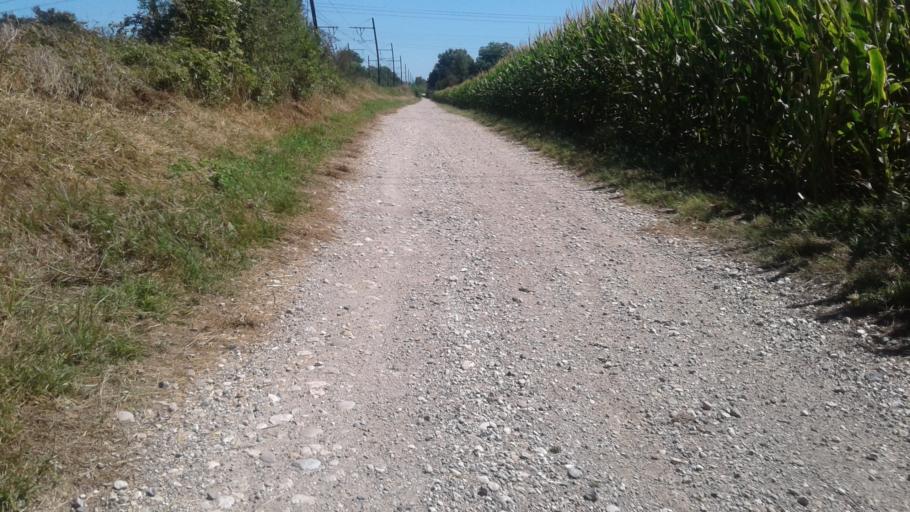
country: FR
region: Rhone-Alpes
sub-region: Departement de l'Ain
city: La Boisse
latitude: 45.8372
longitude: 5.0231
